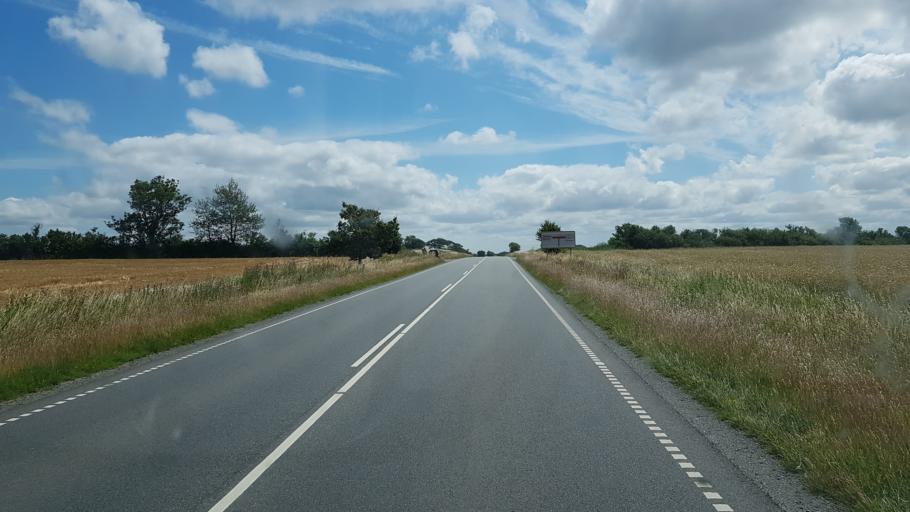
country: DK
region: South Denmark
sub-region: Vejen Kommune
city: Rodding
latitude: 55.3741
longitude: 9.0731
